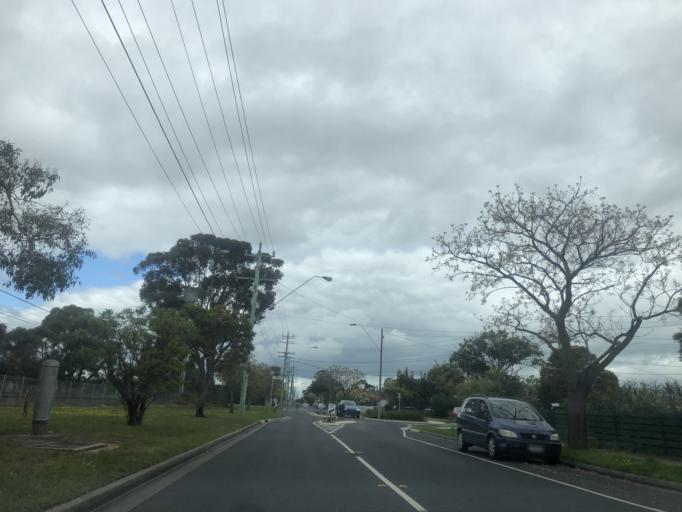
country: AU
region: Victoria
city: Clayton
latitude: -37.9195
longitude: 145.1133
